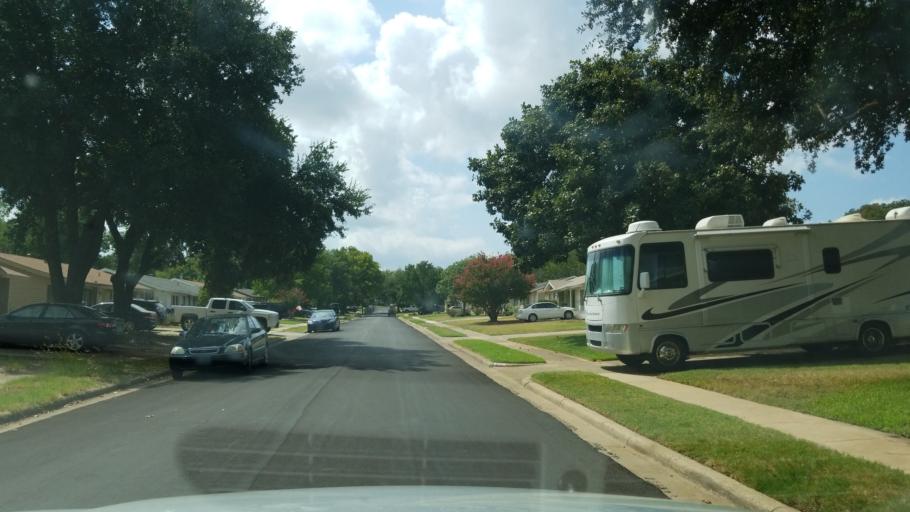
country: US
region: Texas
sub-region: Tarrant County
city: Euless
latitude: 32.8450
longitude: -97.0884
